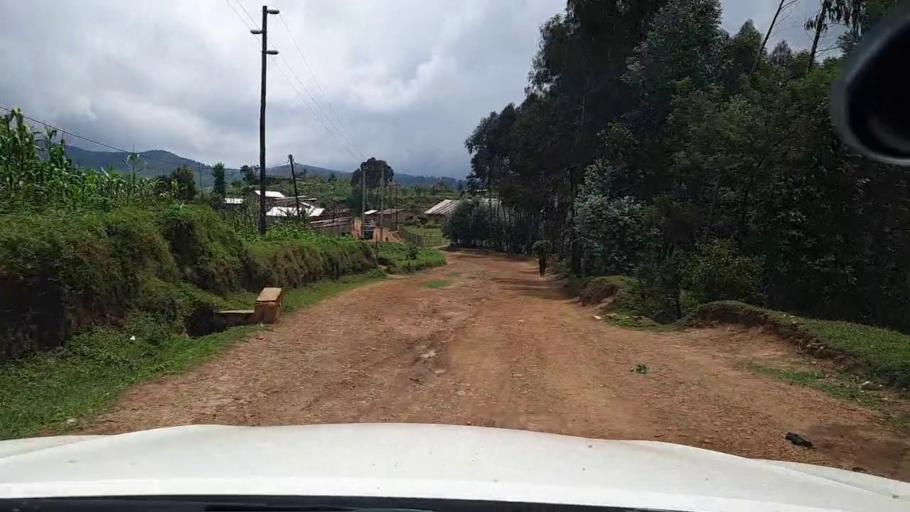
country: RW
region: Western Province
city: Kibuye
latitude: -2.1690
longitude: 29.4290
